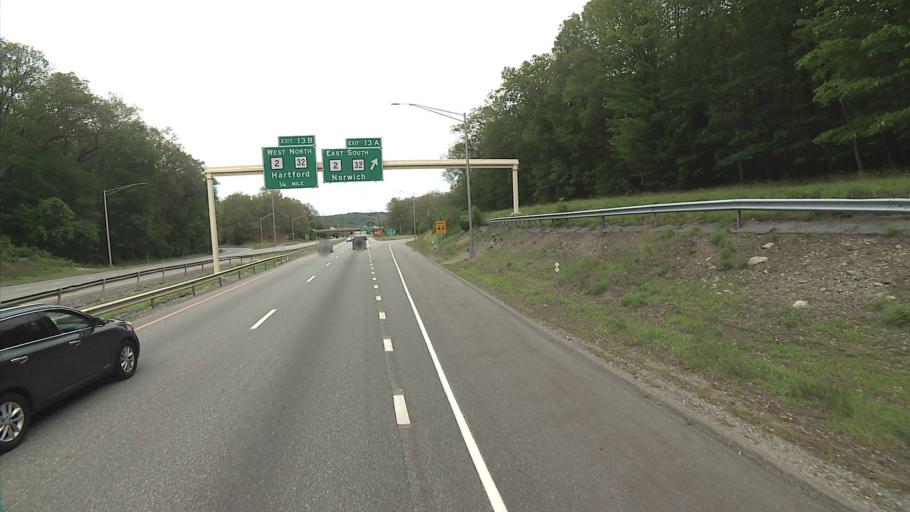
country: US
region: Connecticut
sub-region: New London County
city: Norwich
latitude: 41.5432
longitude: -72.1102
